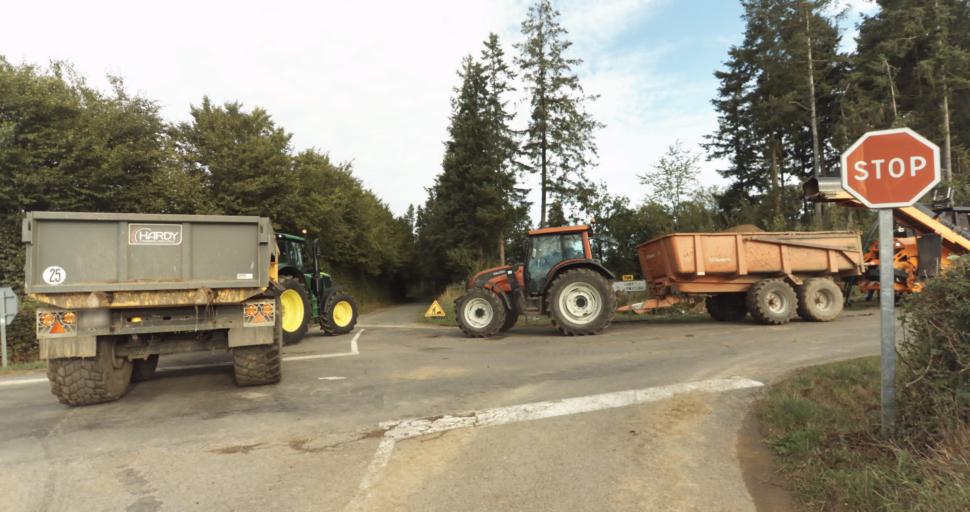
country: FR
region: Lower Normandy
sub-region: Departement de l'Orne
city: Gace
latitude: 48.8457
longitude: 0.2497
